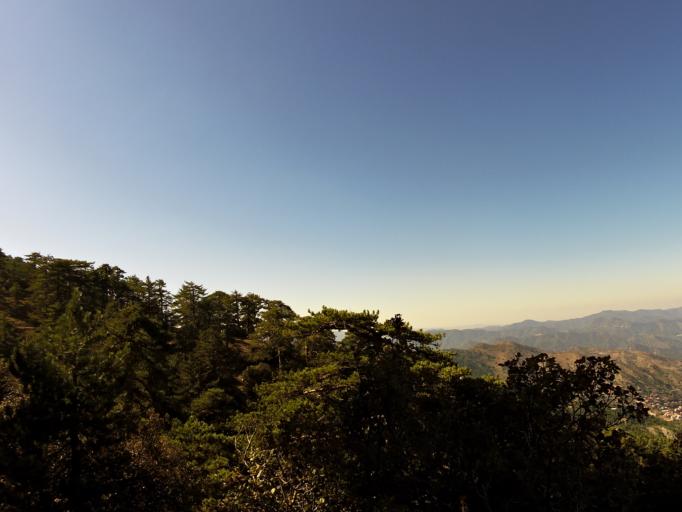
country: CY
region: Lefkosia
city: Kakopetria
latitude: 34.9579
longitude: 32.8540
